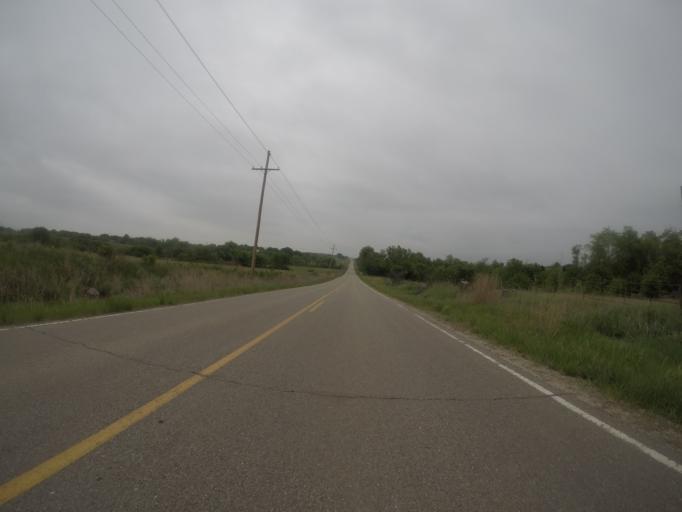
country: US
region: Kansas
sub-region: Pottawatomie County
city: Westmoreland
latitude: 39.5222
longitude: -96.2683
